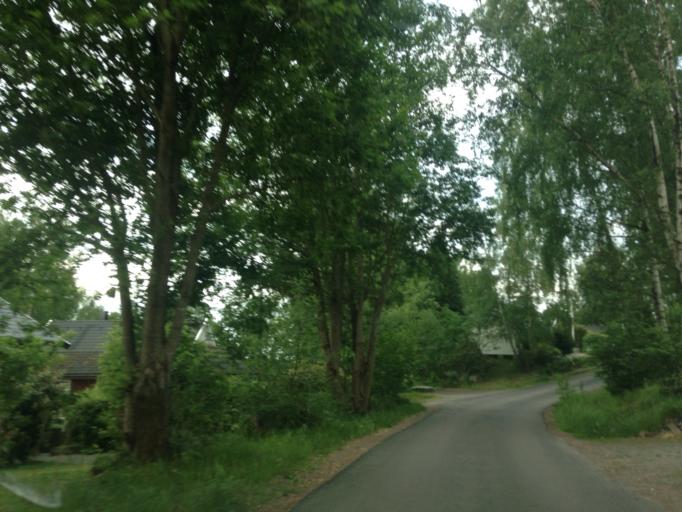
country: SE
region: Vaestra Goetaland
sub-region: Goteborg
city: Torslanda
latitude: 57.7759
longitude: 11.8475
